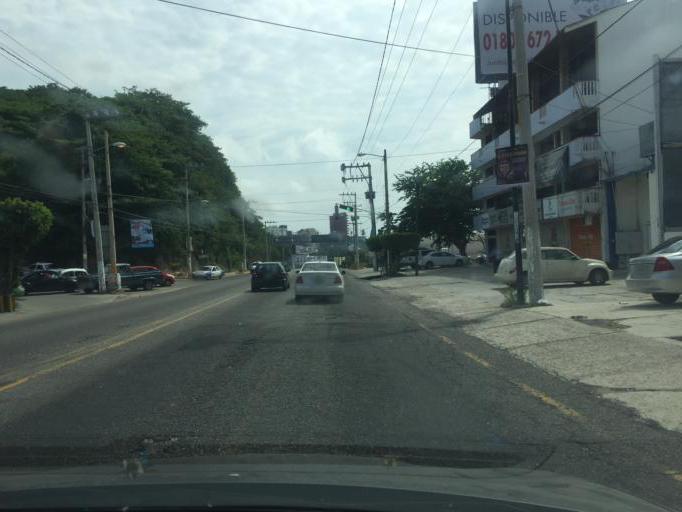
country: MX
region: Guerrero
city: Acapulco de Juarez
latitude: 16.8670
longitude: -99.8693
